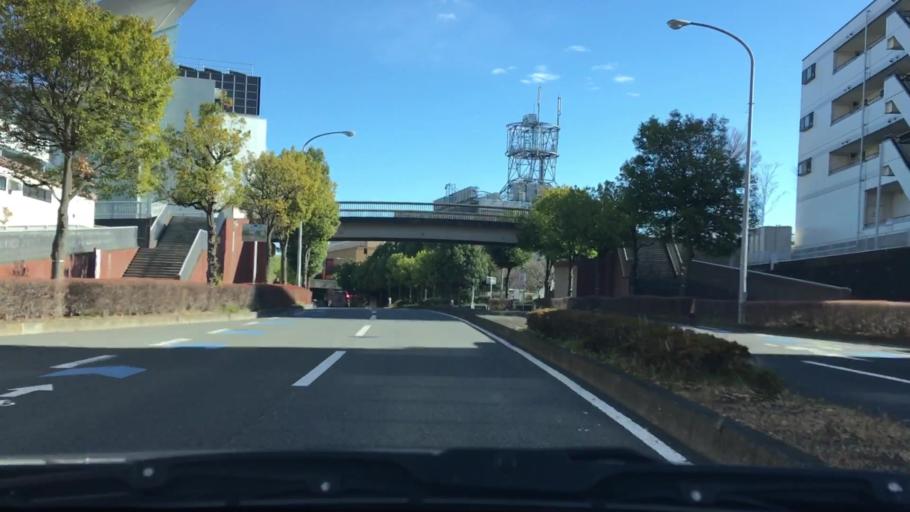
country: JP
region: Kanagawa
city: Yokohama
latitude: 35.5418
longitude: 139.5718
